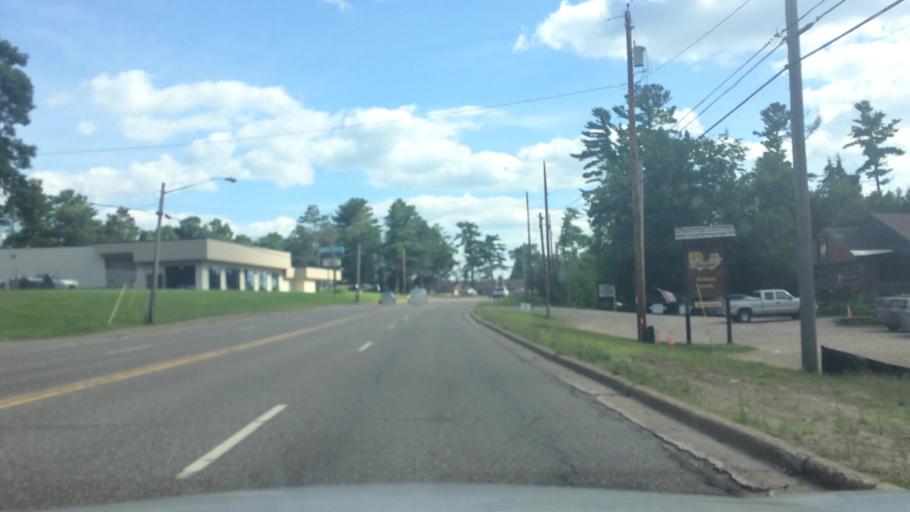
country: US
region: Wisconsin
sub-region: Vilas County
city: Lac du Flambeau
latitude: 45.9090
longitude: -89.6948
